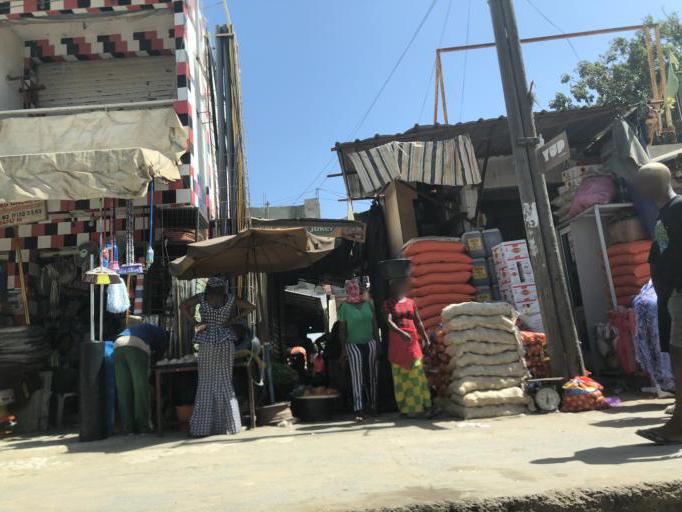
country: SN
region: Dakar
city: Mermoz Boabab
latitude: 14.7237
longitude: -17.4879
